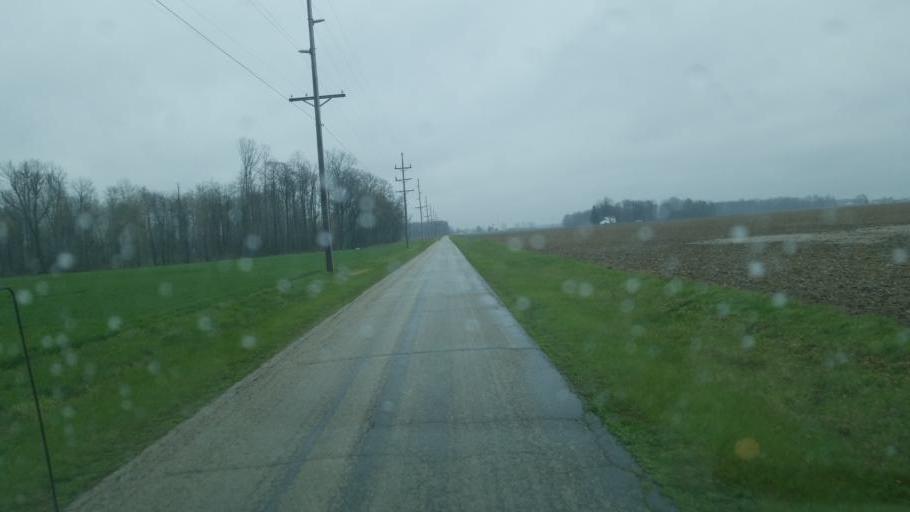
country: US
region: Ohio
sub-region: Crawford County
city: Bucyrus
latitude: 40.8340
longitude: -83.0829
